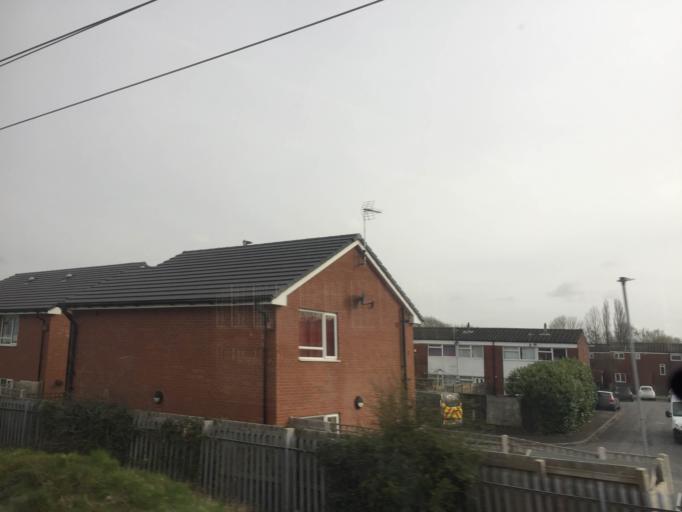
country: GB
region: England
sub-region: Lancashire
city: Coppull
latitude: 53.6270
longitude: -2.6606
